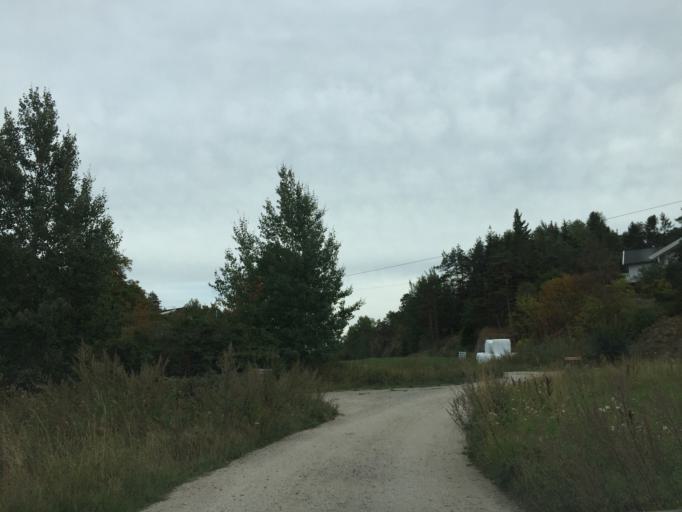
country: NO
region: Ostfold
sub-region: Hvaler
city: Skjaerhalden
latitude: 59.0361
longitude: 11.0535
